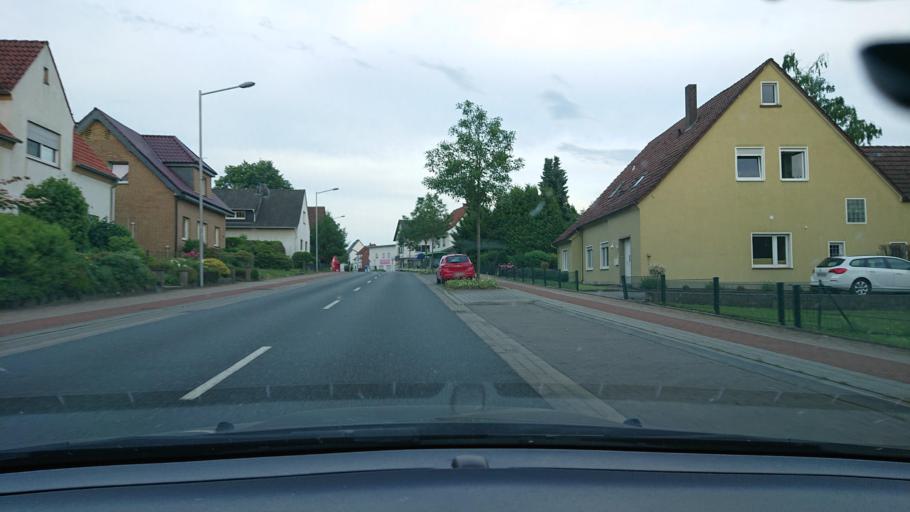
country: DE
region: North Rhine-Westphalia
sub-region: Regierungsbezirk Detmold
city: Hiddenhausen
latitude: 52.1687
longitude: 8.6271
